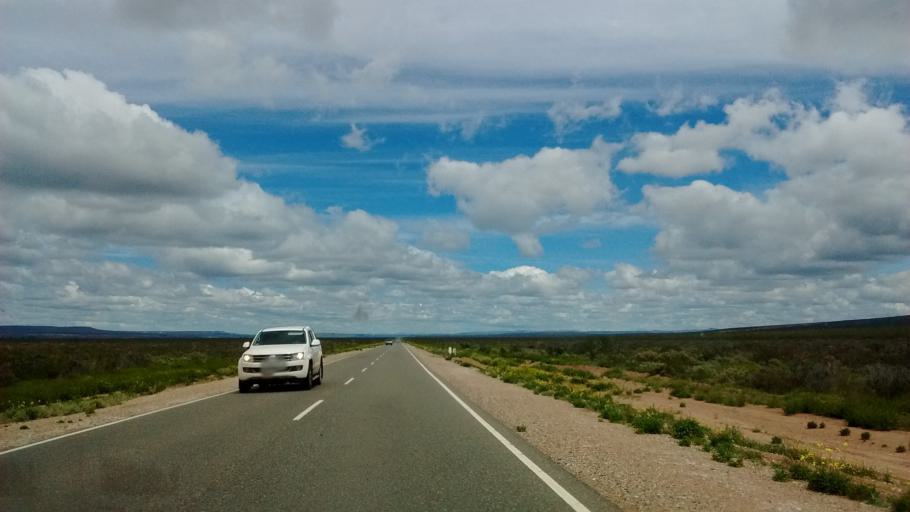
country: AR
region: Neuquen
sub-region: Departamento de Picun Leufu
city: Picun Leufu
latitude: -39.7880
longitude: -69.6681
